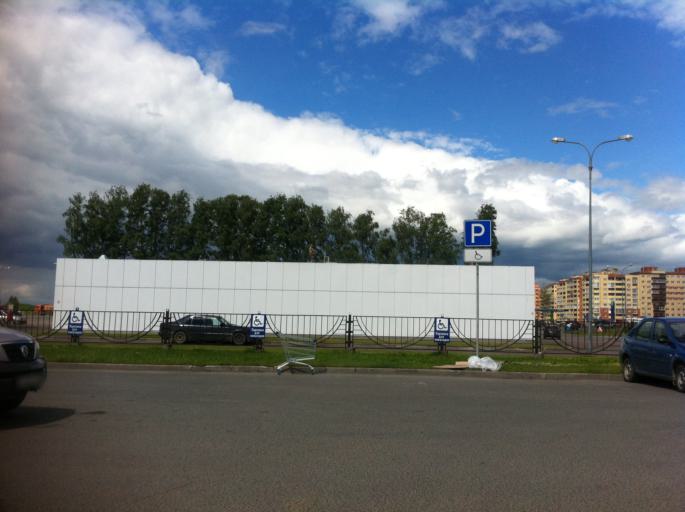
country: RU
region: Pskov
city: Pskov
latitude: 57.8057
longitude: 28.2673
